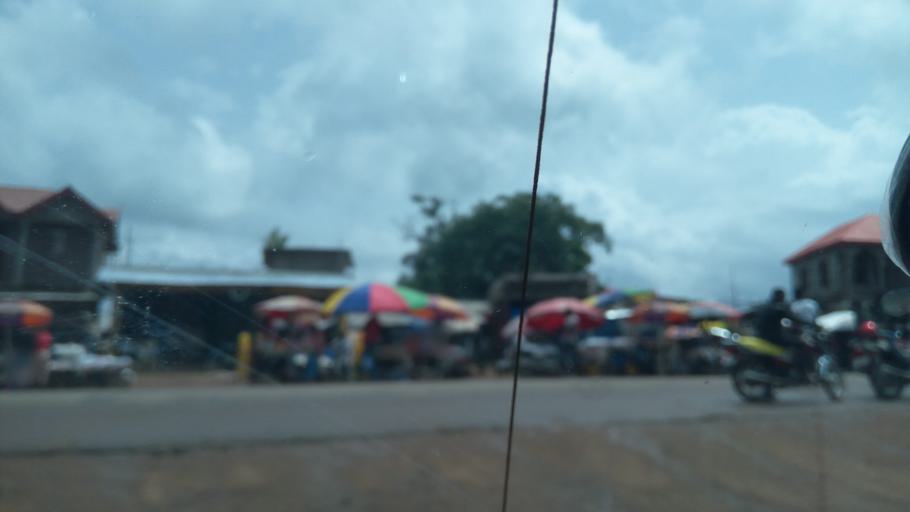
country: SL
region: Northern Province
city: Kambia
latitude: 9.0371
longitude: -12.9076
